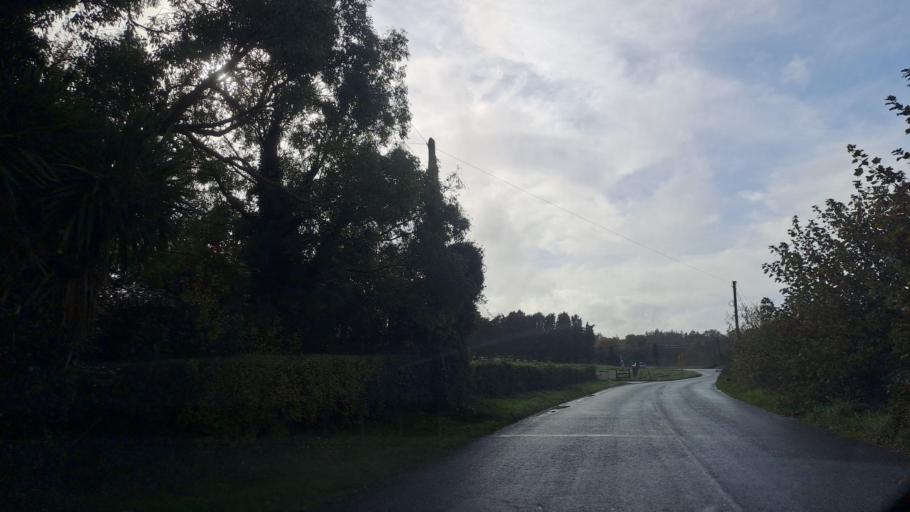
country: IE
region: Ulster
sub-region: County Monaghan
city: Carrickmacross
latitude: 53.9532
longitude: -6.7151
